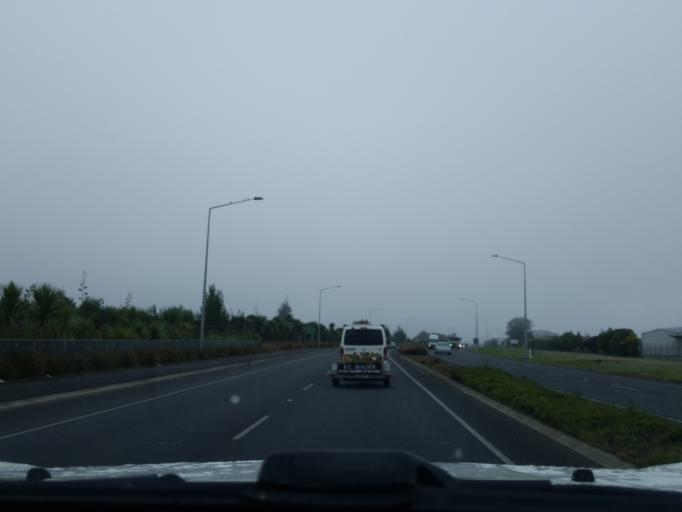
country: NZ
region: Waikato
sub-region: Hamilton City
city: Hamilton
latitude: -37.7656
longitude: 175.2363
